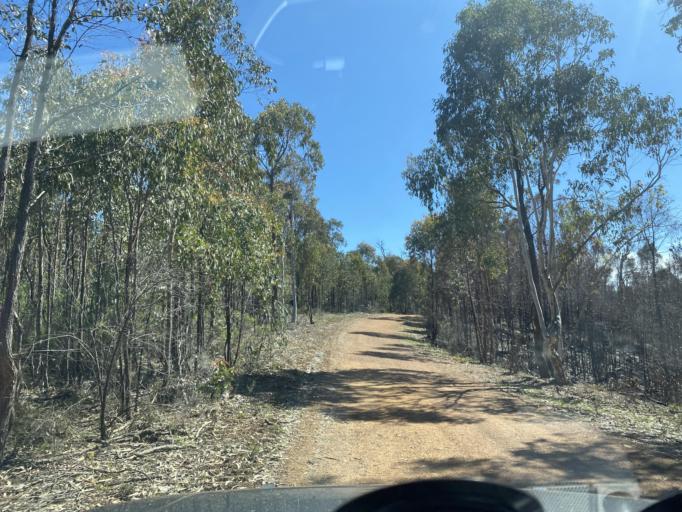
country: AU
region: Victoria
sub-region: Benalla
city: Benalla
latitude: -36.7359
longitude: 146.1822
